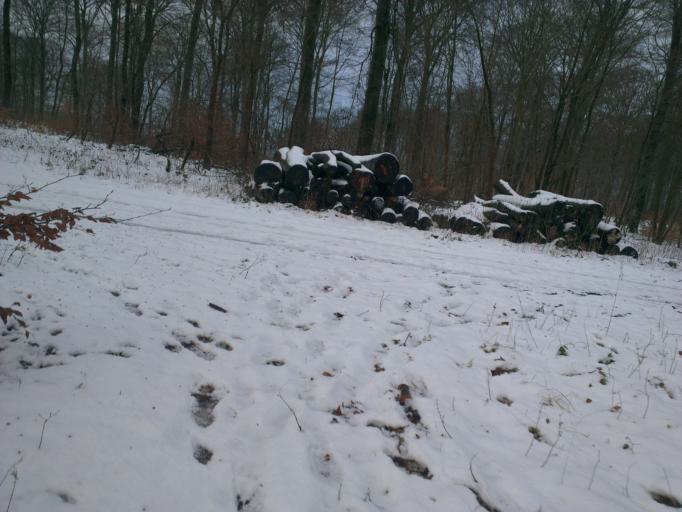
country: DK
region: Capital Region
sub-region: Frederikssund Kommune
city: Frederikssund
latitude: 55.8505
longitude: 12.0228
